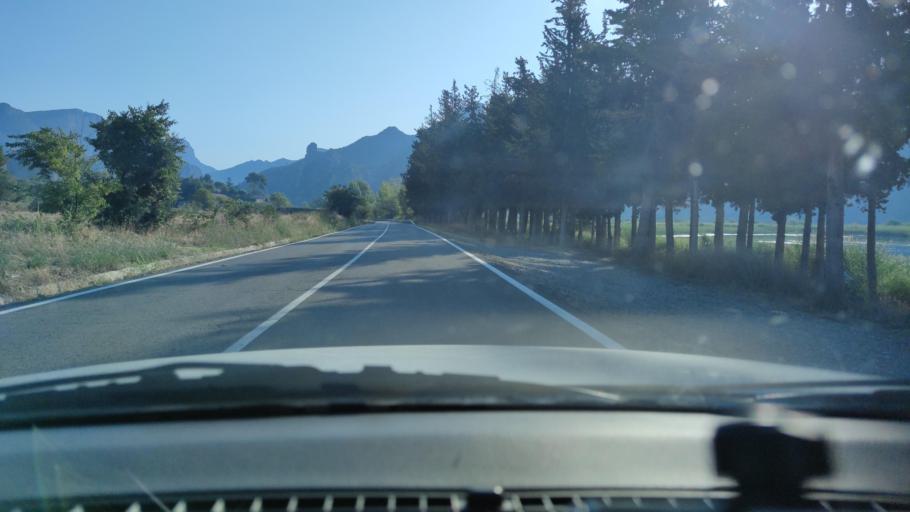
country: ES
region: Catalonia
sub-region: Provincia de Lleida
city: Camarasa
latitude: 41.8614
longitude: 0.8348
